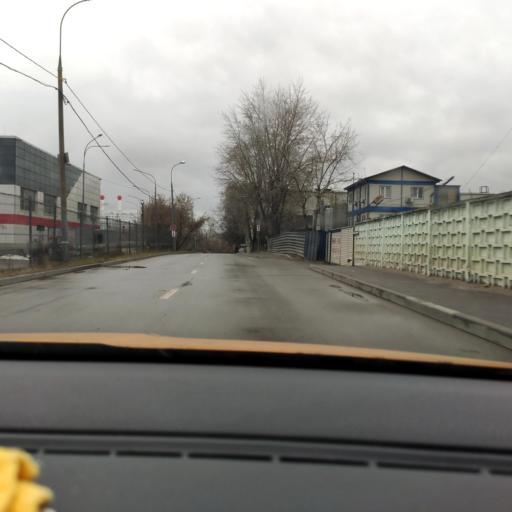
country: RU
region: Moscow
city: Ryazanskiy
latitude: 55.7396
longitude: 37.7316
